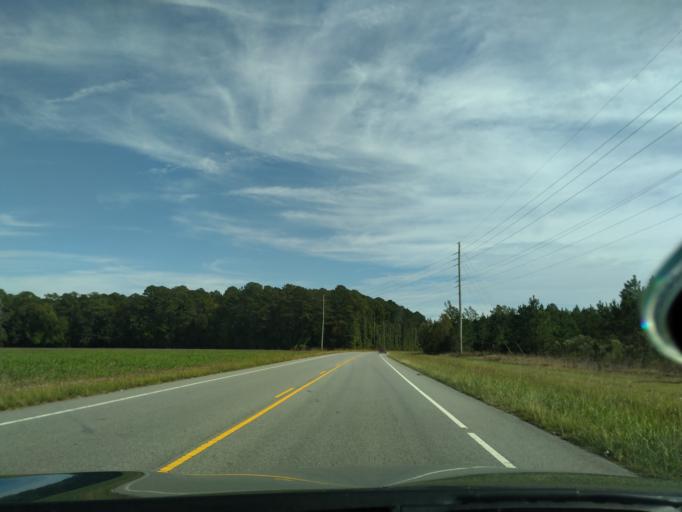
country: US
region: North Carolina
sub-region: Beaufort County
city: River Road
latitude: 35.5213
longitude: -76.9297
